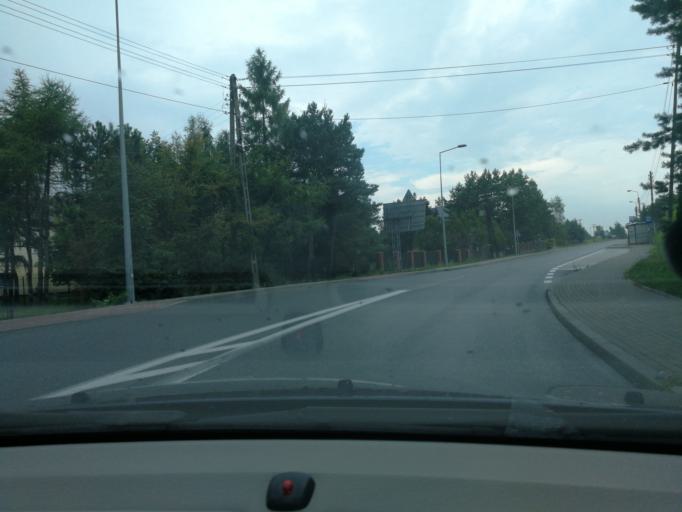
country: PL
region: Masovian Voivodeship
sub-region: Powiat zyrardowski
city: Radziejowice
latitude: 52.0048
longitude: 20.5558
